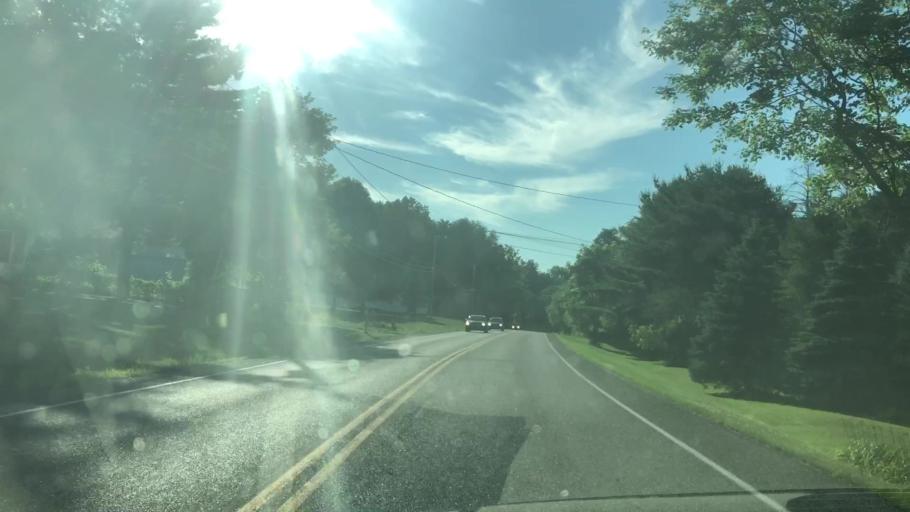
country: US
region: New York
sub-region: Ontario County
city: Victor
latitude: 43.0275
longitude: -77.4247
